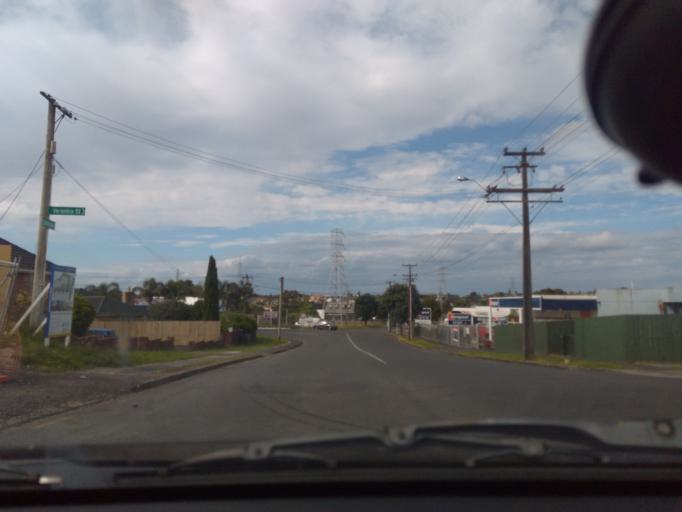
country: NZ
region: Auckland
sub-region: Auckland
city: Waitakere
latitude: -36.9041
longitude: 174.6843
